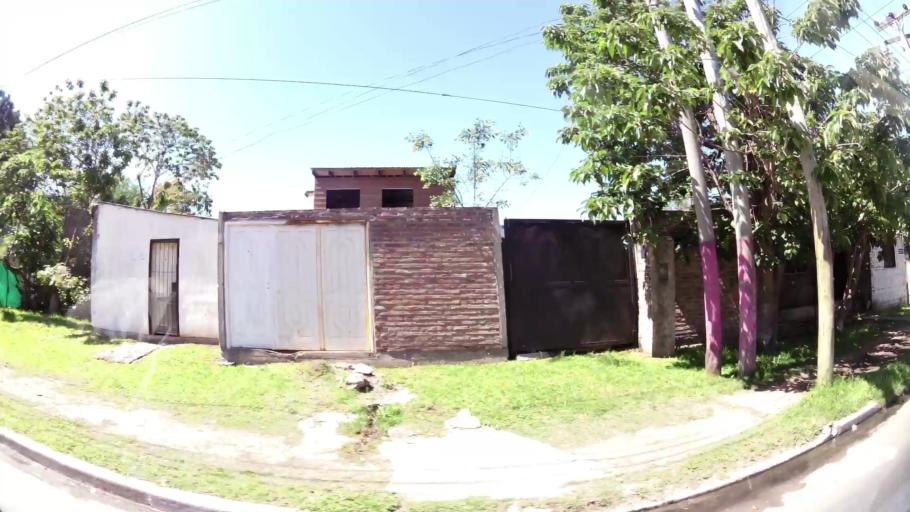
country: AR
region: Buenos Aires
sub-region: Partido de Quilmes
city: Quilmes
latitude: -34.7248
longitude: -58.2914
